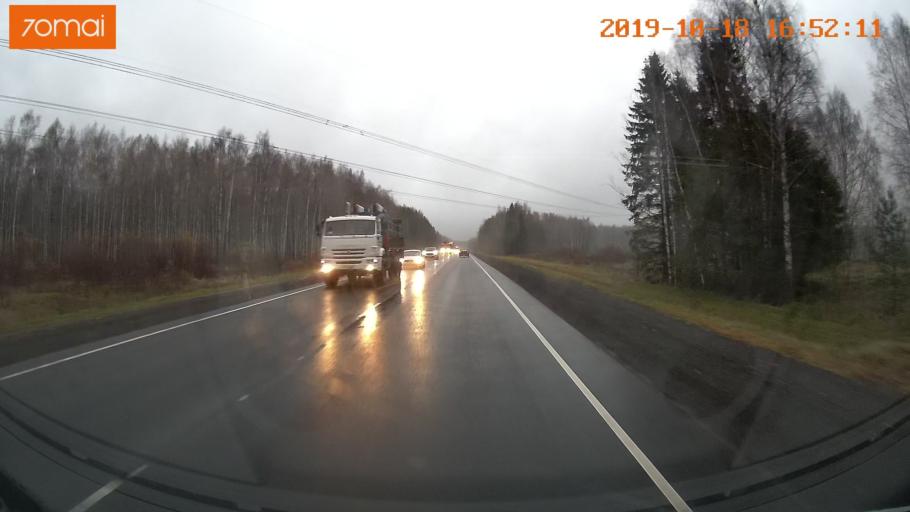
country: RU
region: Vladimir
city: Kideksha
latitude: 56.5968
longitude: 40.5557
